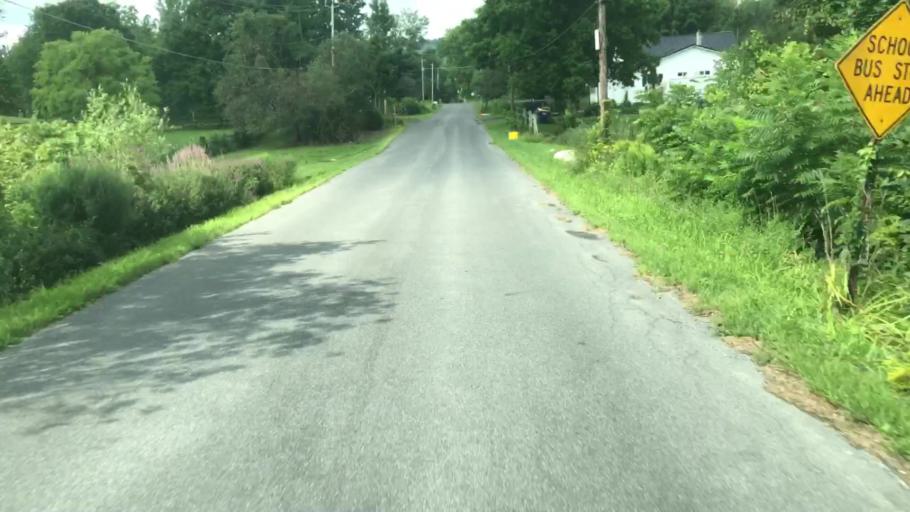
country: US
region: New York
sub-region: Onondaga County
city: Camillus
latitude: 43.0614
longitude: -76.3546
